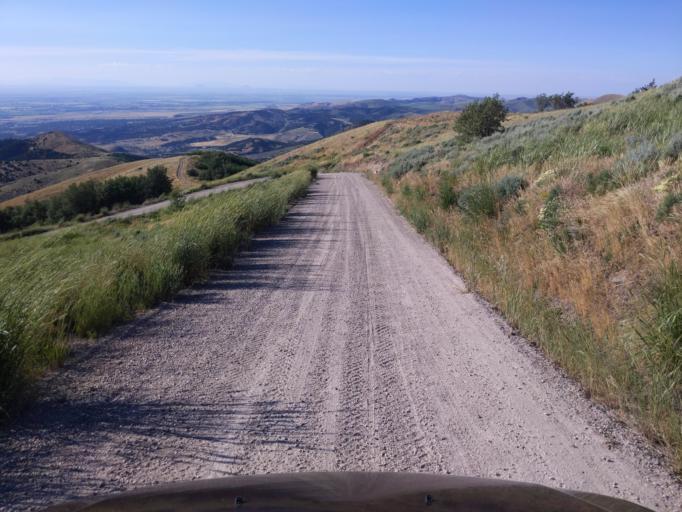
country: US
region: Idaho
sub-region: Bannock County
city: Pocatello
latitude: 42.8511
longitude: -112.3624
